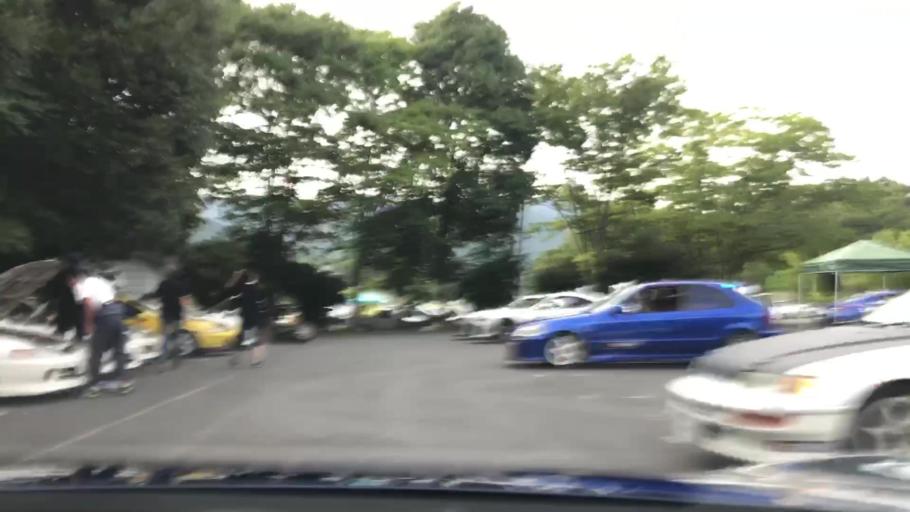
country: JP
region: Ibaraki
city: Makabe
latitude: 36.2390
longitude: 140.1696
